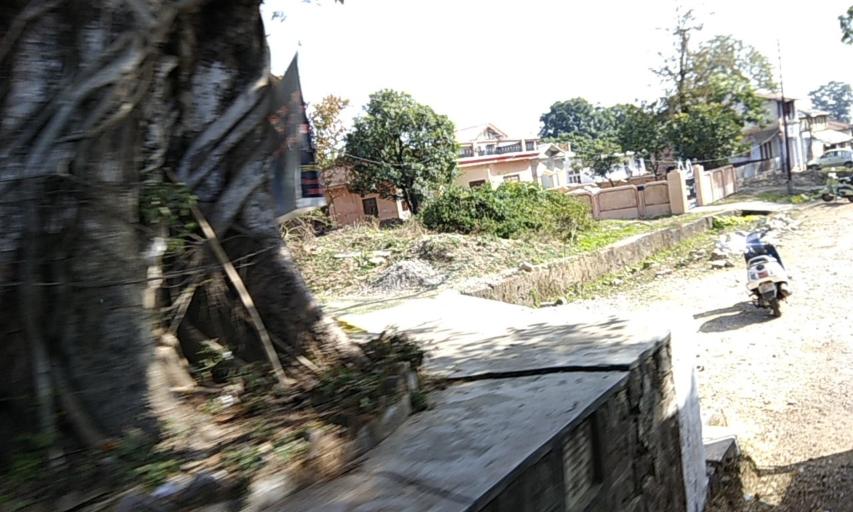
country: IN
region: Himachal Pradesh
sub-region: Kangra
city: Yol
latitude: 32.2186
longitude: 76.1776
